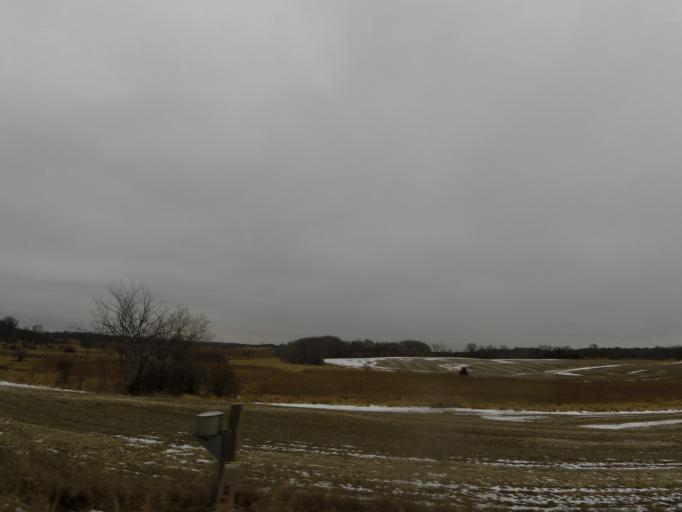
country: US
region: Minnesota
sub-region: Carver County
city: Watertown
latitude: 44.9892
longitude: -93.8489
